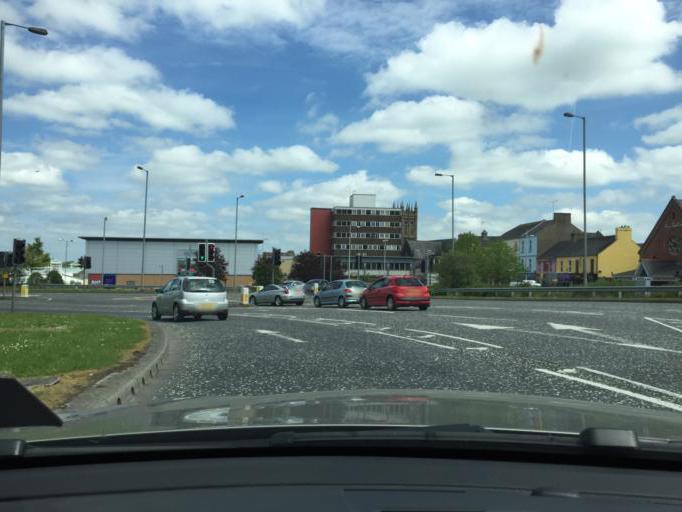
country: GB
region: Northern Ireland
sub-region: Armagh District
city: Portadown
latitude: 54.4223
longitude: -6.4491
